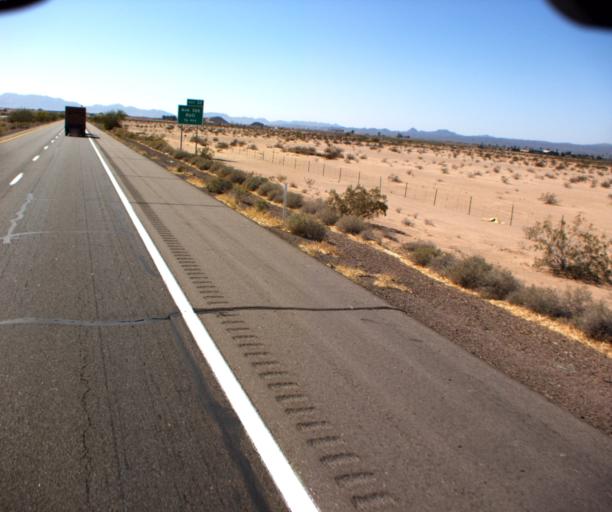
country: US
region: Arizona
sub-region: Yuma County
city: Wellton
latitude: 32.6846
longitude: -114.0081
